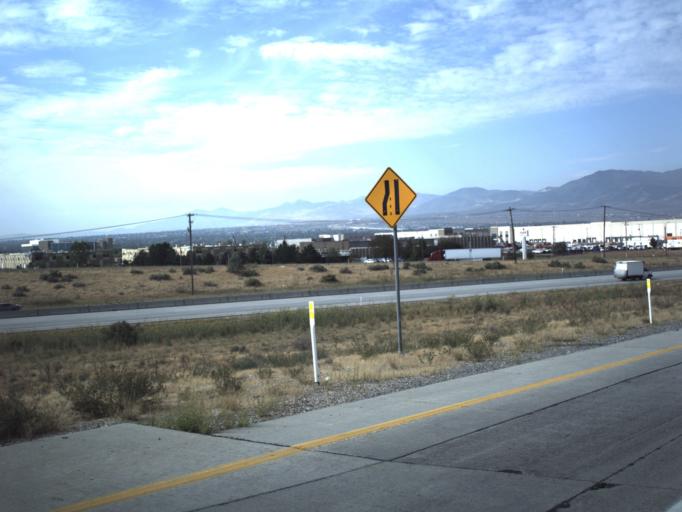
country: US
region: Utah
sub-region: Salt Lake County
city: West Valley City
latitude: 40.7268
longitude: -111.9872
